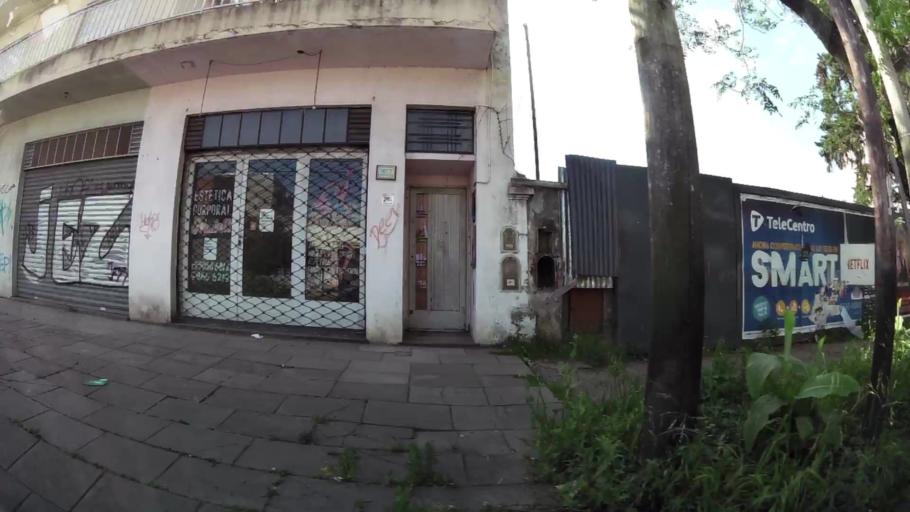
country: AR
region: Buenos Aires
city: San Justo
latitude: -34.6556
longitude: -58.5794
